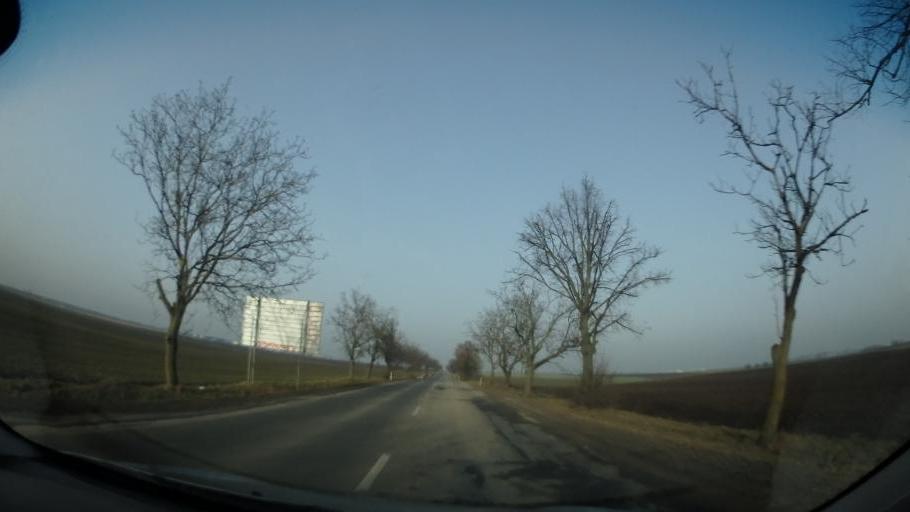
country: CZ
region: South Moravian
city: Rajhrad
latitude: 49.0703
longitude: 16.5752
